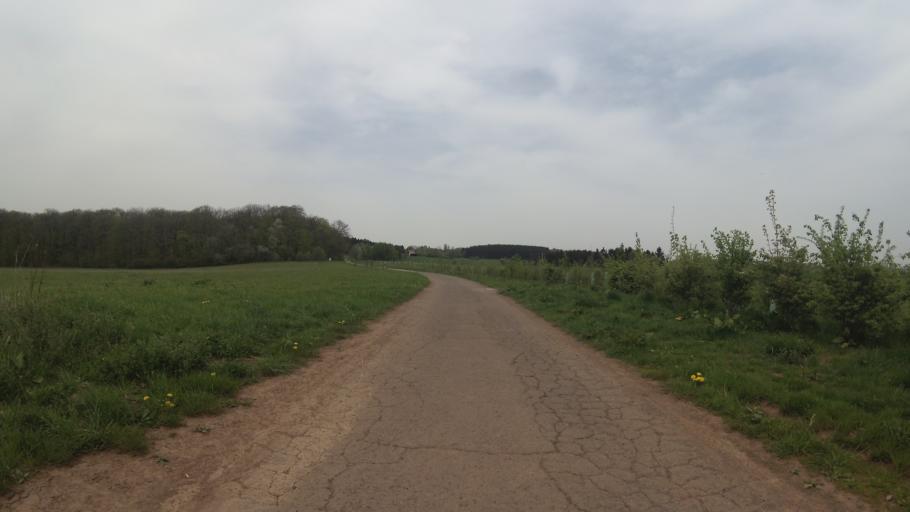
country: DE
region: Saarland
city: Schiffweiler
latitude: 49.3875
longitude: 7.1408
